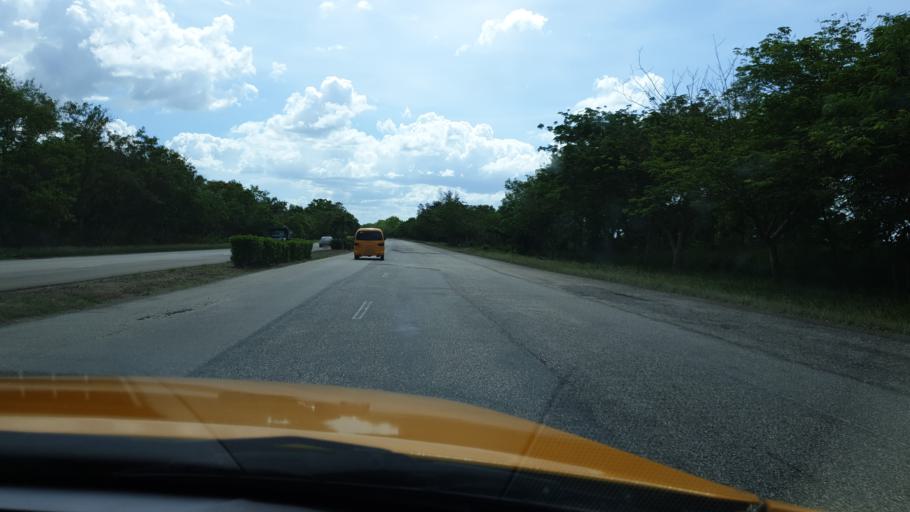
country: CU
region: Cienfuegos
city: Cruces
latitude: 22.4547
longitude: -80.3024
